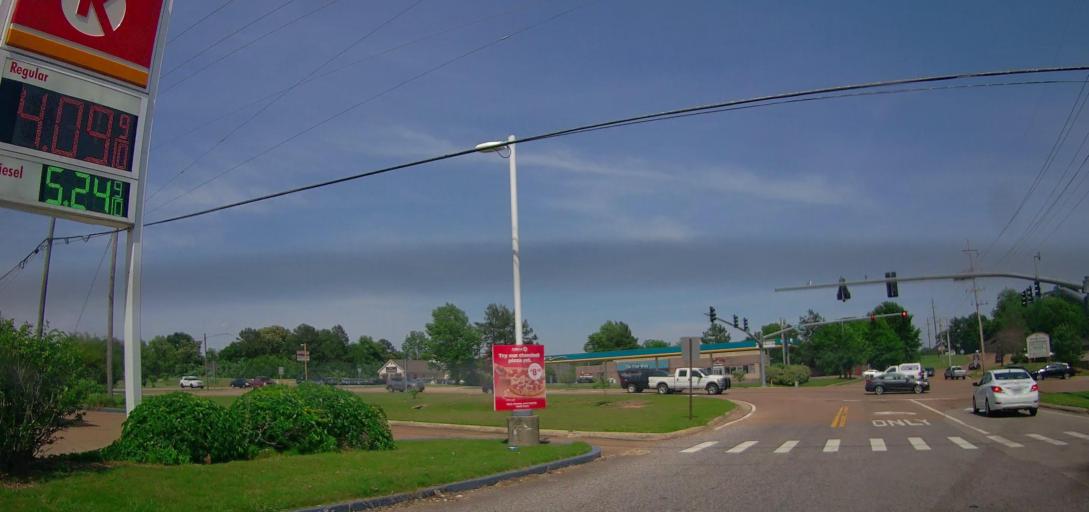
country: US
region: Mississippi
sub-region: De Soto County
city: Olive Branch
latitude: 34.9480
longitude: -89.8311
